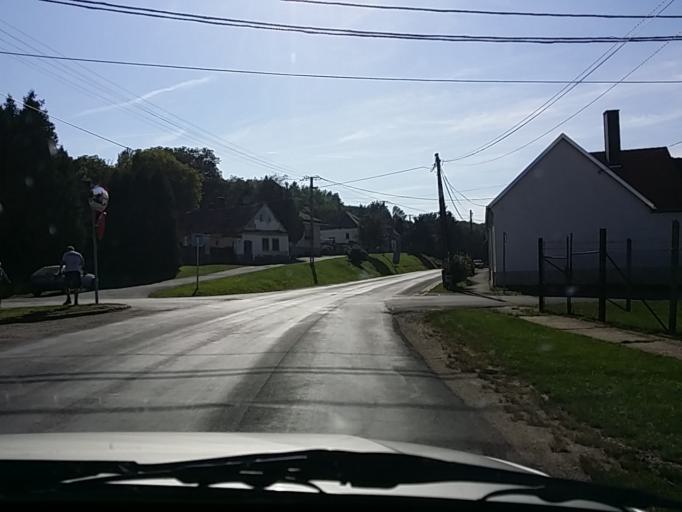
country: AT
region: Burgenland
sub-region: Politischer Bezirk Oberpullendorf
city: Lutzmannsburg
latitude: 47.4248
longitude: 16.6487
